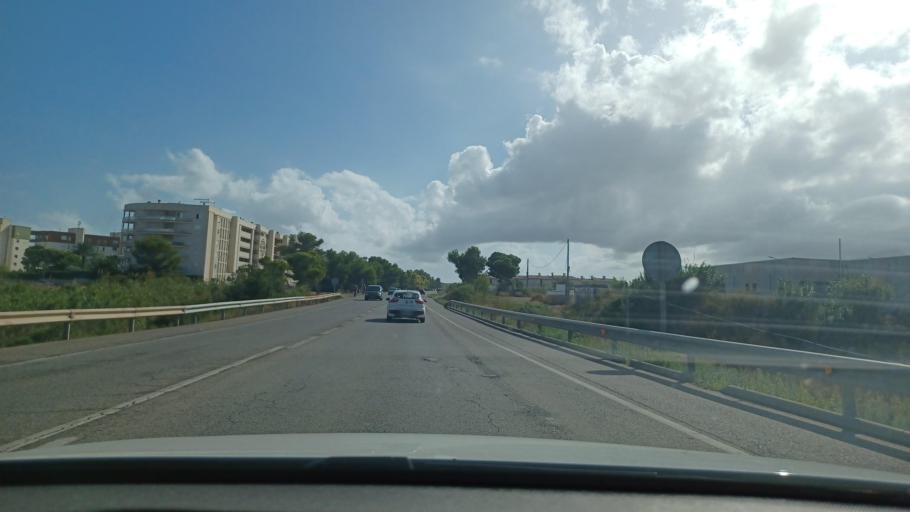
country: ES
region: Catalonia
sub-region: Provincia de Tarragona
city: Vilanova d'Escornalbou
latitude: 41.0221
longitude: 0.9545
